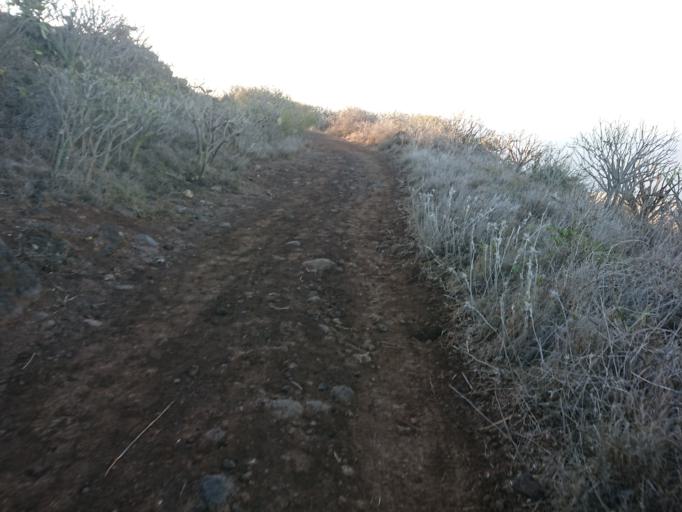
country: ES
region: Canary Islands
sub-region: Provincia de Santa Cruz de Tenerife
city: Tazacorte
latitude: 28.6586
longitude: -17.9450
